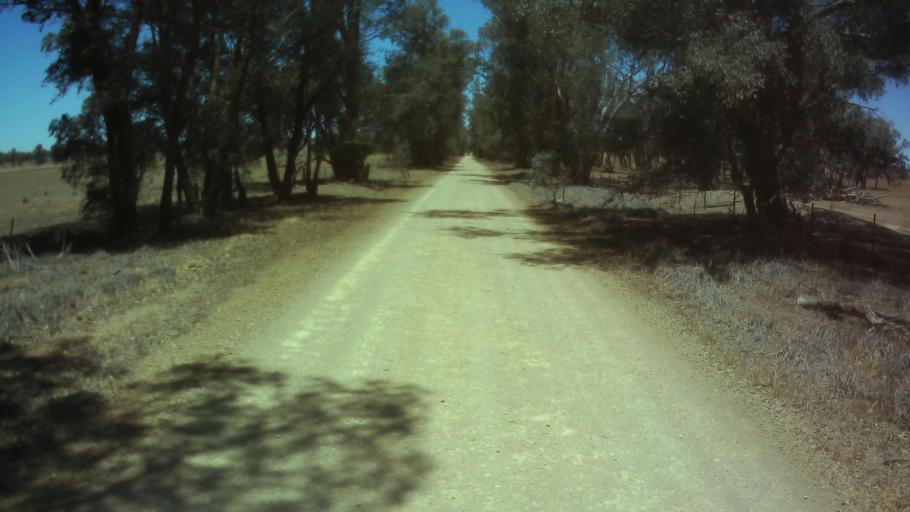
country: AU
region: New South Wales
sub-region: Weddin
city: Grenfell
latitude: -33.9154
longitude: 148.2134
